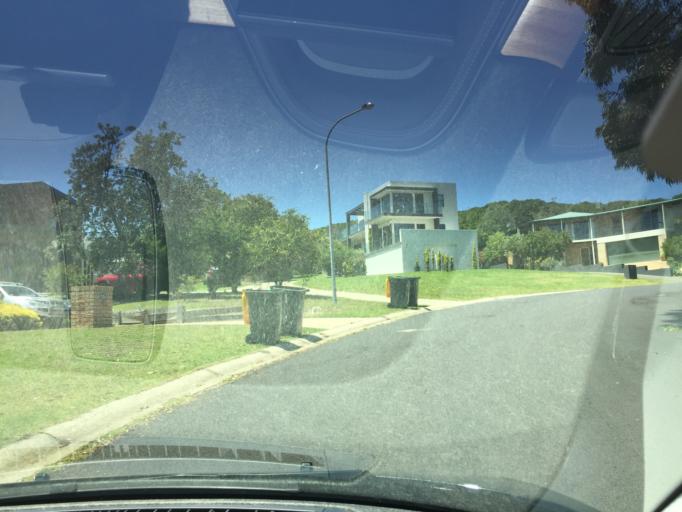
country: AU
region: New South Wales
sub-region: Bega Valley
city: Merimbula
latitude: -36.8485
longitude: 149.9344
